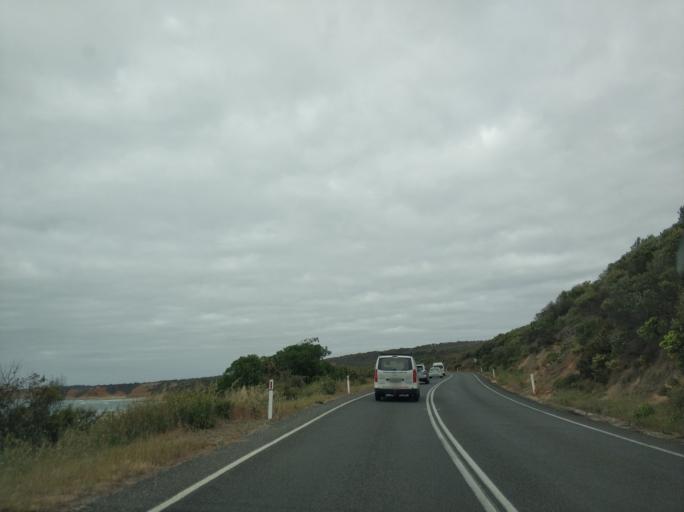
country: AU
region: Victoria
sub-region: Surf Coast
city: Anglesea
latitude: -38.4310
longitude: 144.1414
